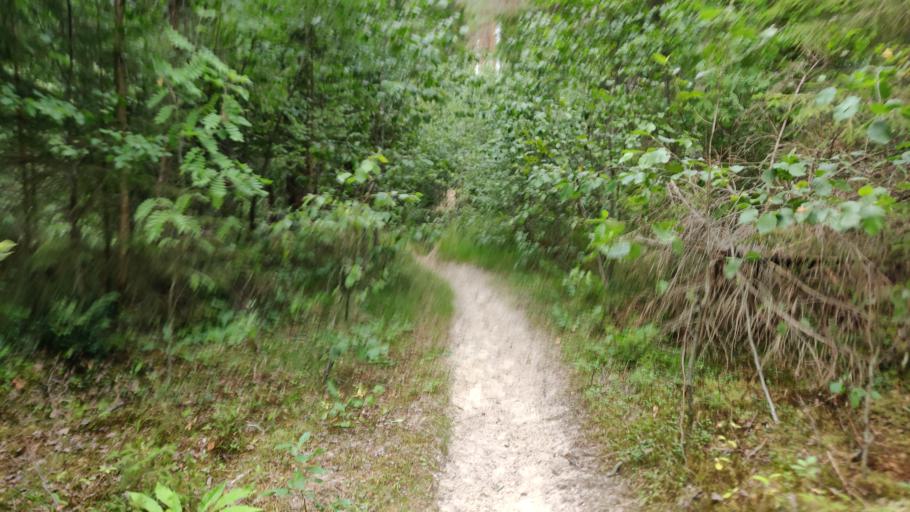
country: SE
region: Vaermland
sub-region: Hagfors Kommun
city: Hagfors
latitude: 60.0321
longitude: 13.5463
